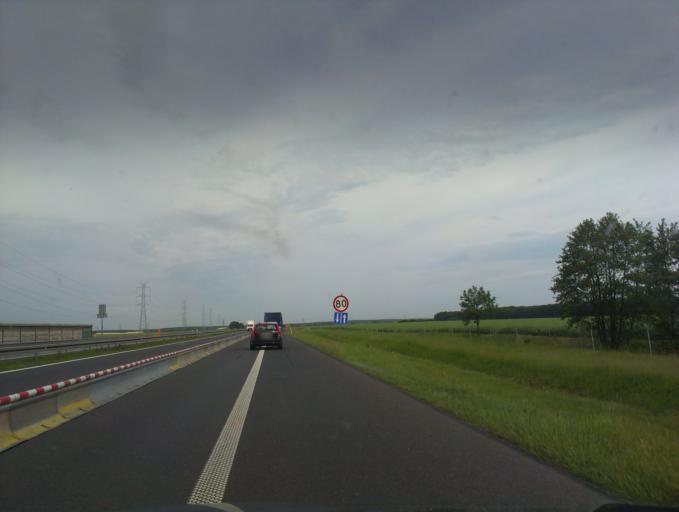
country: PL
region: Opole Voivodeship
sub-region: Powiat brzeski
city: Losiow
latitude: 50.7187
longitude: 17.5478
